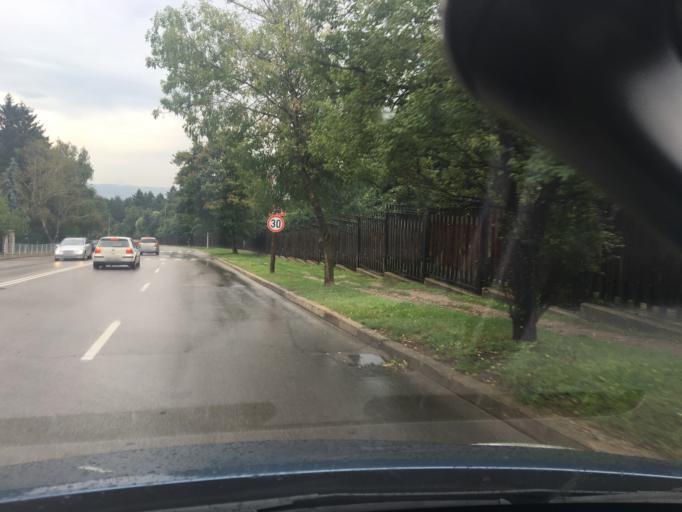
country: BG
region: Sofia-Capital
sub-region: Stolichna Obshtina
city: Sofia
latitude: 42.6502
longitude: 23.2660
